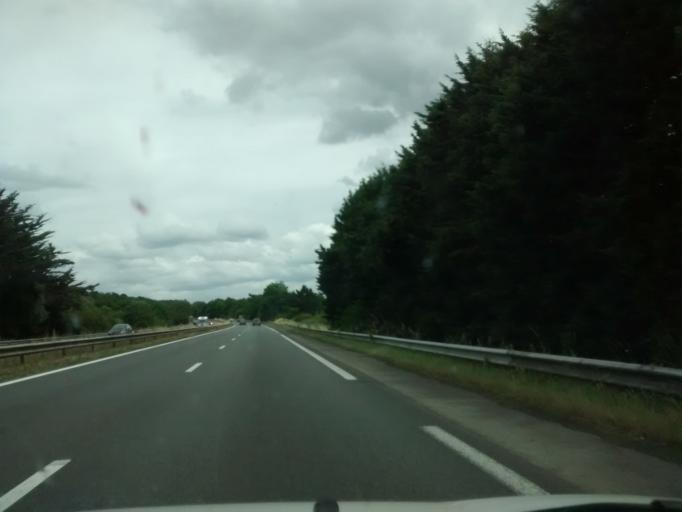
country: FR
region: Brittany
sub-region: Departement des Cotes-d'Armor
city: Yffiniac
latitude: 48.4798
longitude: -2.6725
